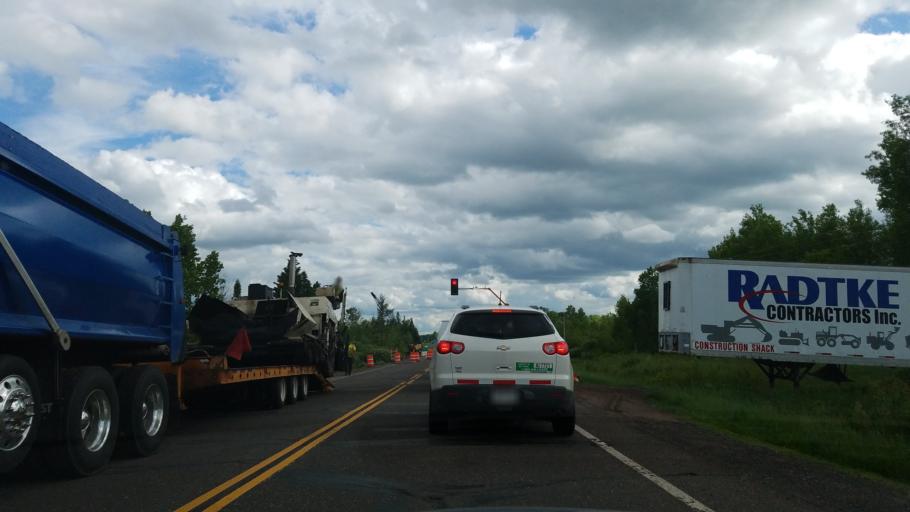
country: US
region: Wisconsin
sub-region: Douglas County
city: Superior
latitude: 46.2361
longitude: -92.1547
